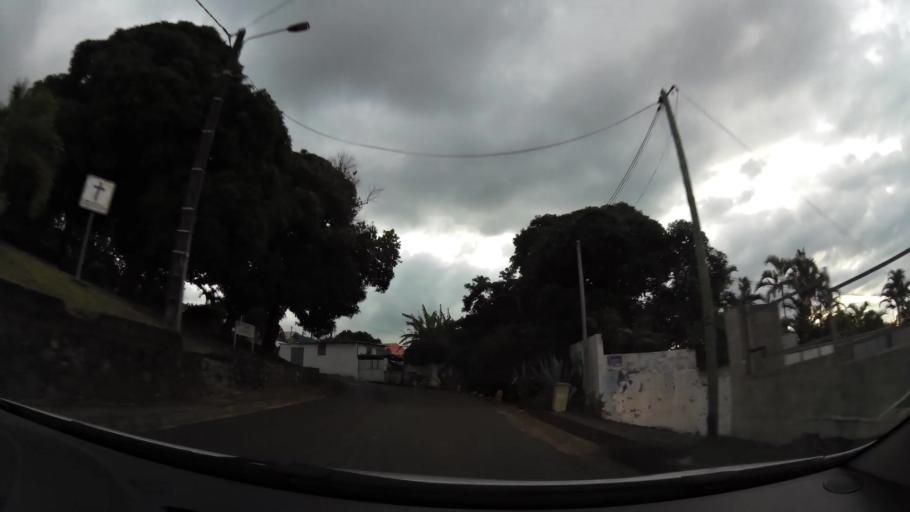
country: RE
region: Reunion
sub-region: Reunion
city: Saint-Denis
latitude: -20.9082
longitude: 55.4666
